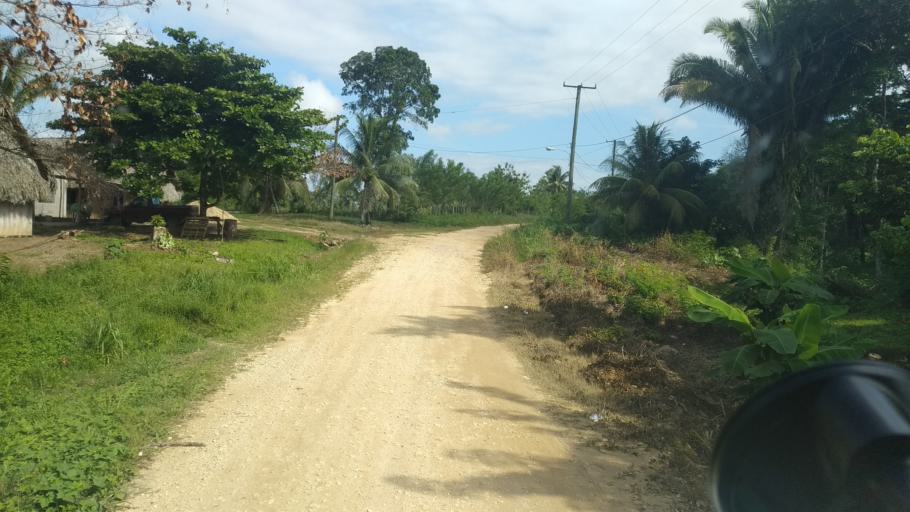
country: BZ
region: Toledo
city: Punta Gorda
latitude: 16.2096
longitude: -88.9130
